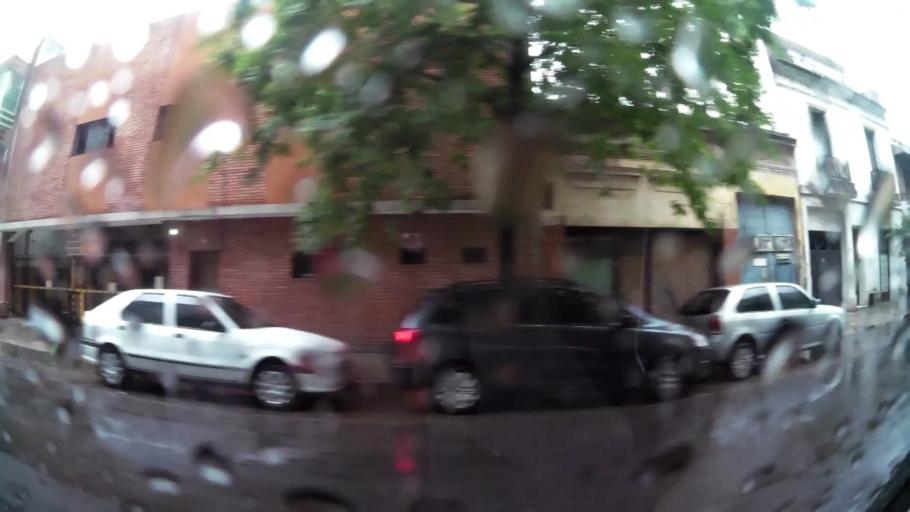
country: AR
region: Buenos Aires F.D.
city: Buenos Aires
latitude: -34.6322
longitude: -58.3726
